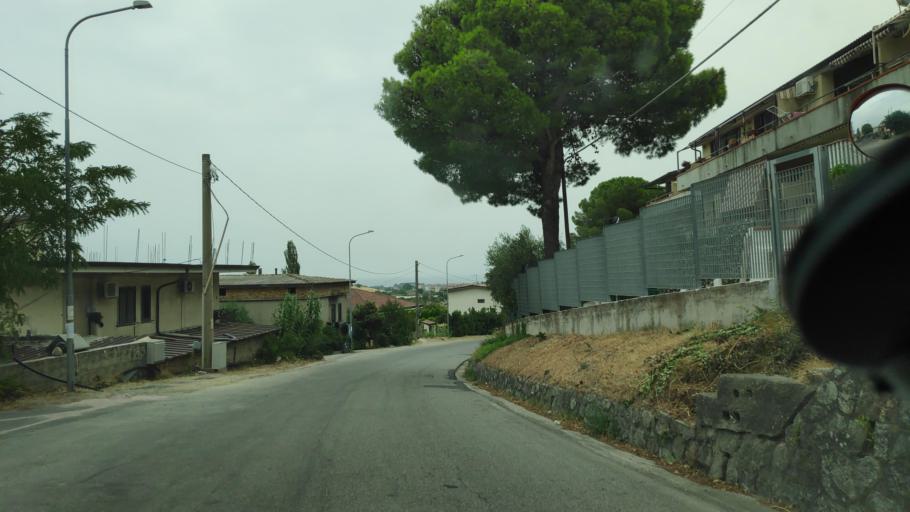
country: IT
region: Calabria
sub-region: Provincia di Catanzaro
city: Martelli-Laganosa
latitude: 38.6673
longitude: 16.5221
